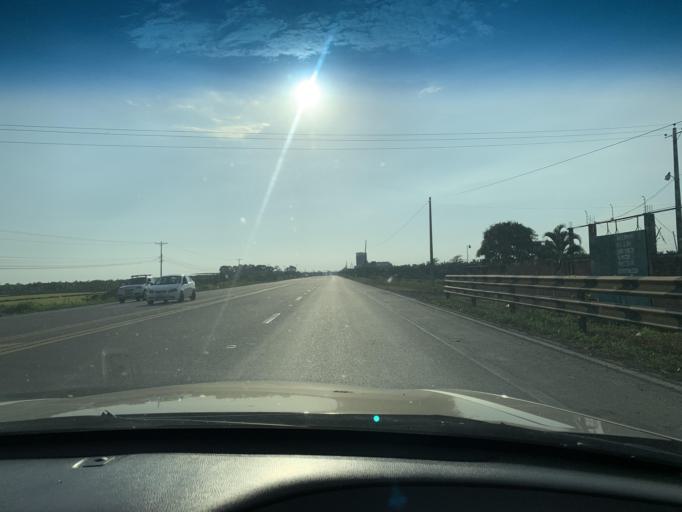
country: EC
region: Guayas
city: Naranjito
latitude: -2.2554
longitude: -79.6072
